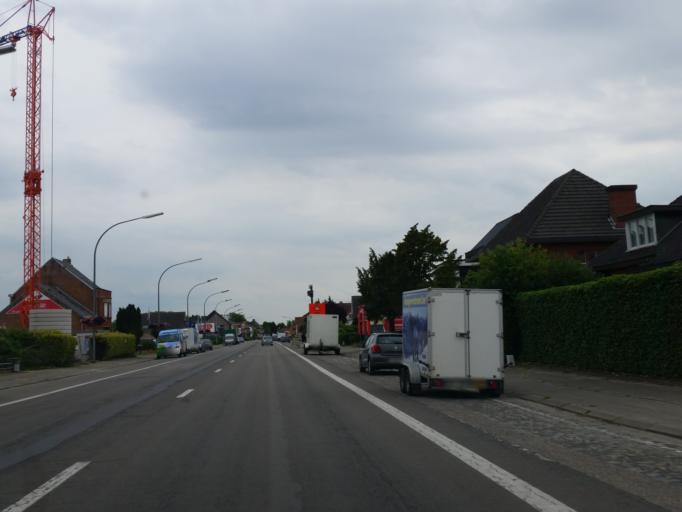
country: BE
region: Flanders
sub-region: Provincie Antwerpen
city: Mechelen
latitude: 51.0504
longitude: 4.4802
